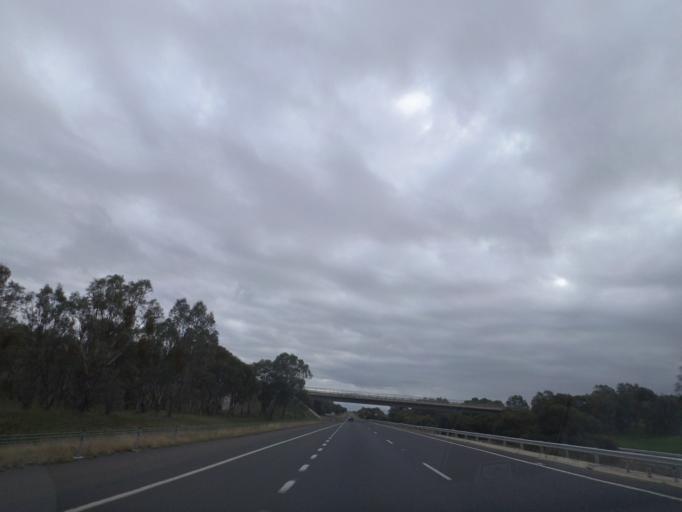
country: AU
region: New South Wales
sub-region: Corowa Shire
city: Howlong
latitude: -36.0828
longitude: 146.7298
